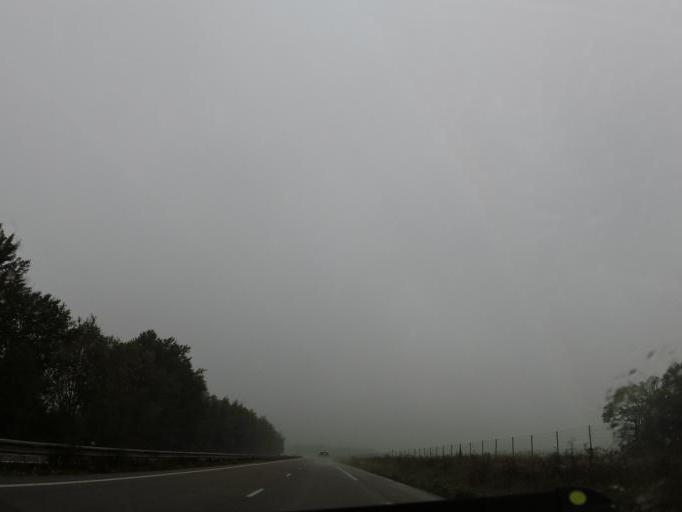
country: FR
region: Picardie
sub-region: Departement de l'Aisne
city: Crezancy
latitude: 49.1098
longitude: 3.4820
